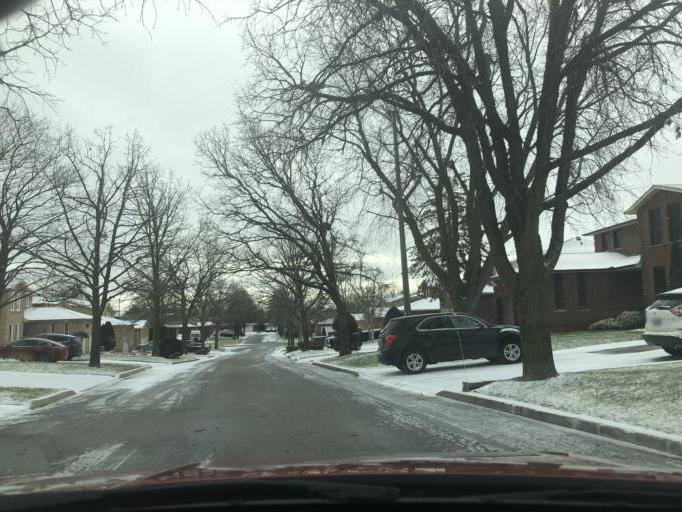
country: CA
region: Ontario
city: Markham
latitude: 43.8742
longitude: -79.2397
